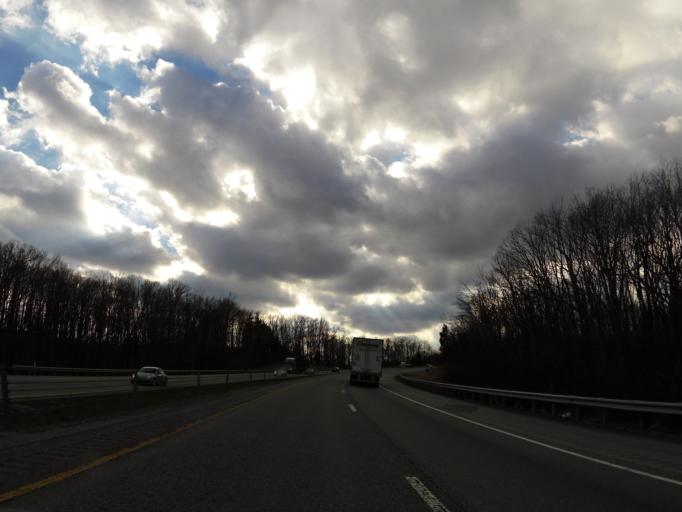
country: US
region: Tennessee
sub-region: Putnam County
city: Monterey
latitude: 36.1360
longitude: -85.3129
